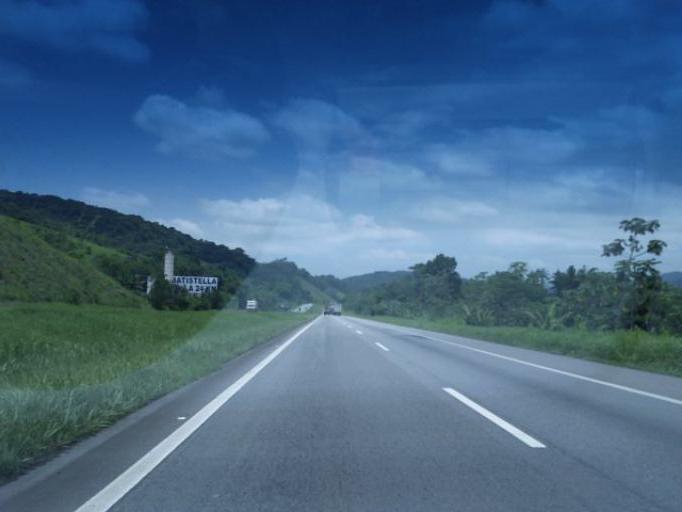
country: BR
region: Sao Paulo
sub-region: Miracatu
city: Miracatu
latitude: -24.1763
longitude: -47.3466
